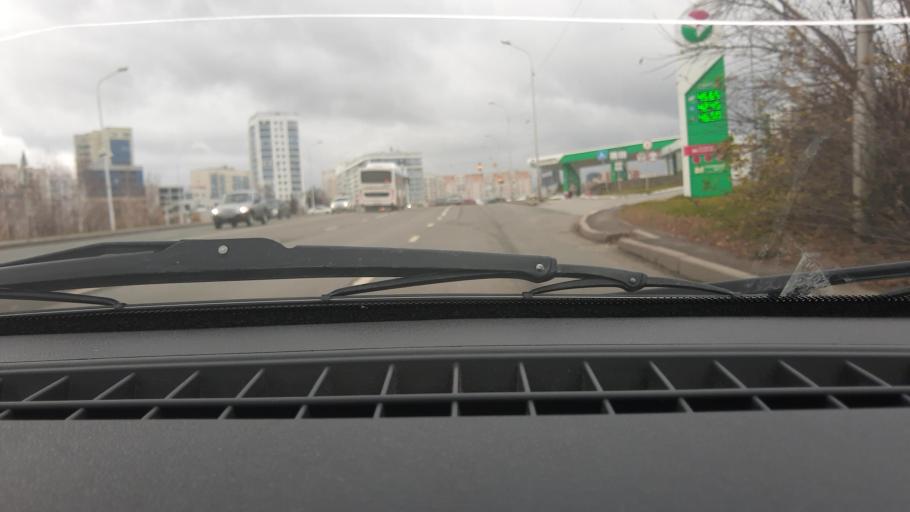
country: RU
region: Bashkortostan
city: Ufa
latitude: 54.7128
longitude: 55.9607
